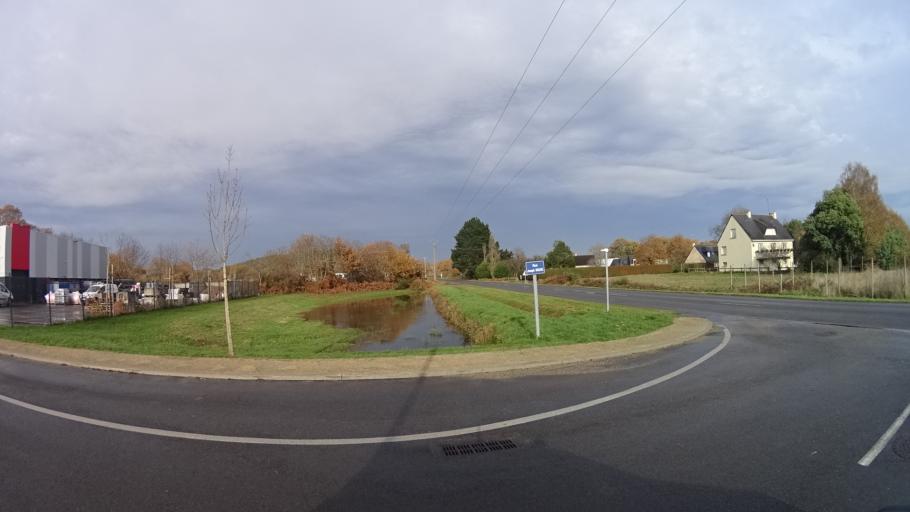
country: FR
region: Brittany
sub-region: Departement du Morbihan
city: Rieux
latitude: 47.6163
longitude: -2.1112
